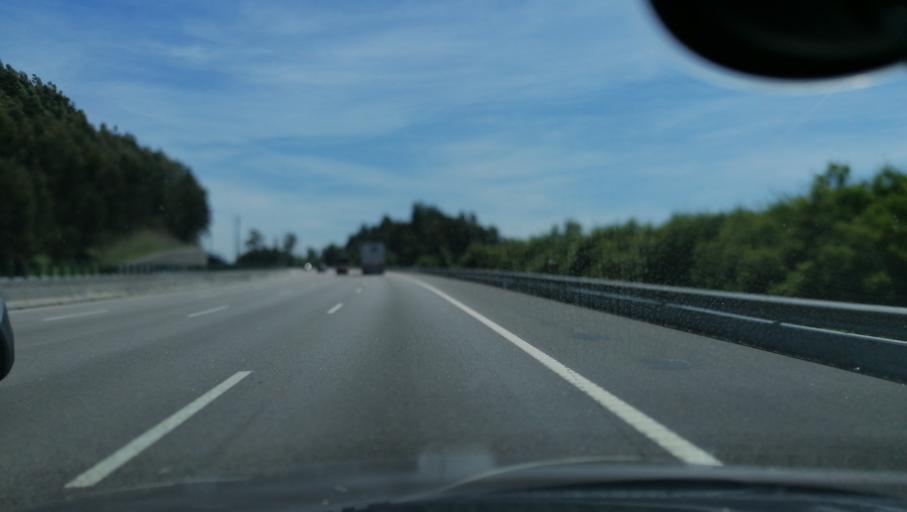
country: PT
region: Porto
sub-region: Vila Nova de Gaia
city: Perozinho
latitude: 41.0579
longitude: -8.5783
